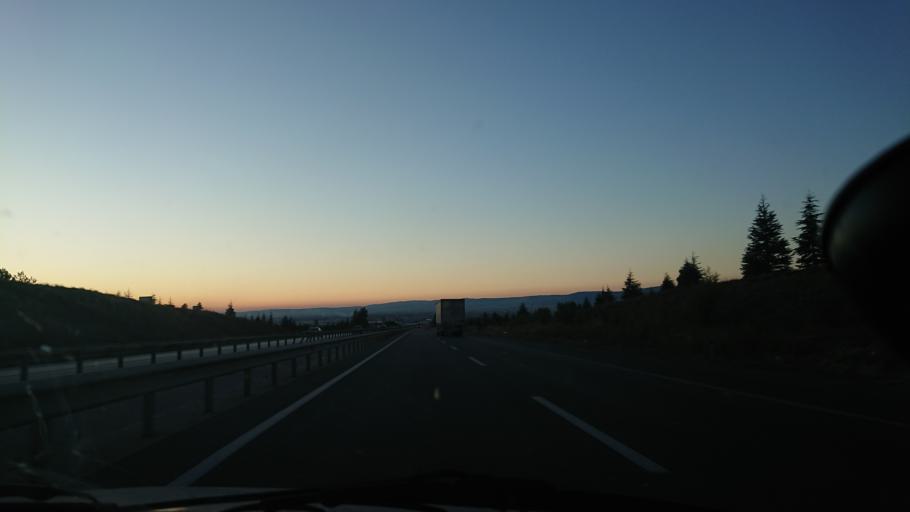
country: TR
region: Eskisehir
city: Sevinc
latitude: 39.7178
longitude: 30.6781
